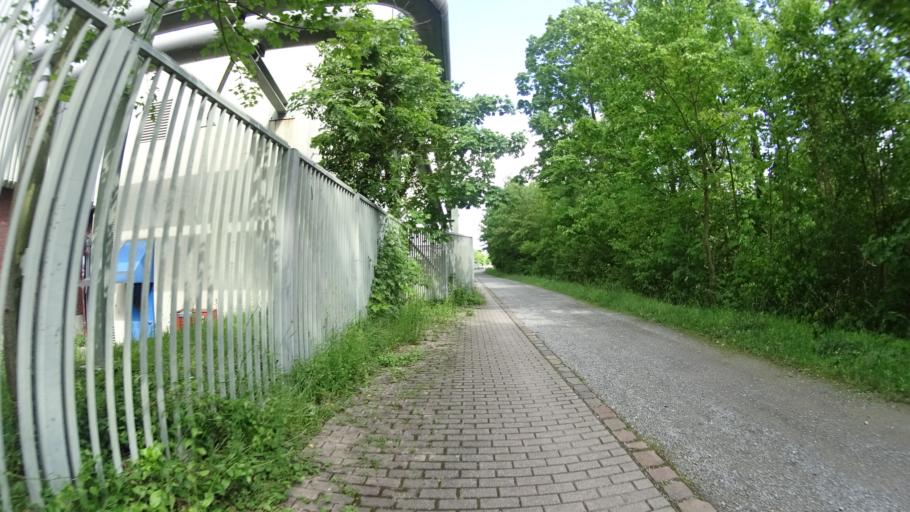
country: DE
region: Baden-Wuerttemberg
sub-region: Karlsruhe Region
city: Rheinstetten
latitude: 49.0115
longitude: 8.3019
